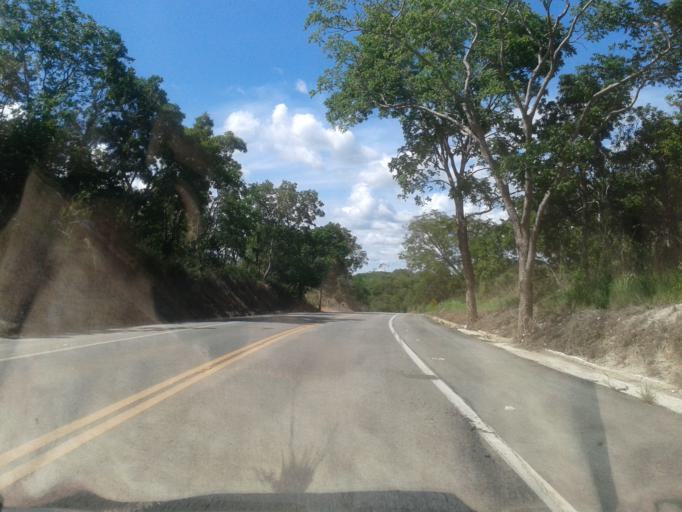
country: BR
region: Goias
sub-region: Goias
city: Goias
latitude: -15.6679
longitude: -50.2156
